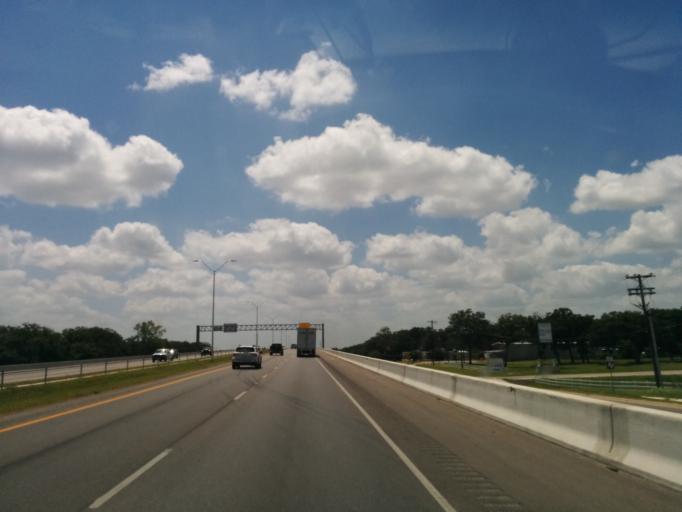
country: US
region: Texas
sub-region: Bastrop County
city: Bastrop
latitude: 30.1112
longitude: -97.3681
